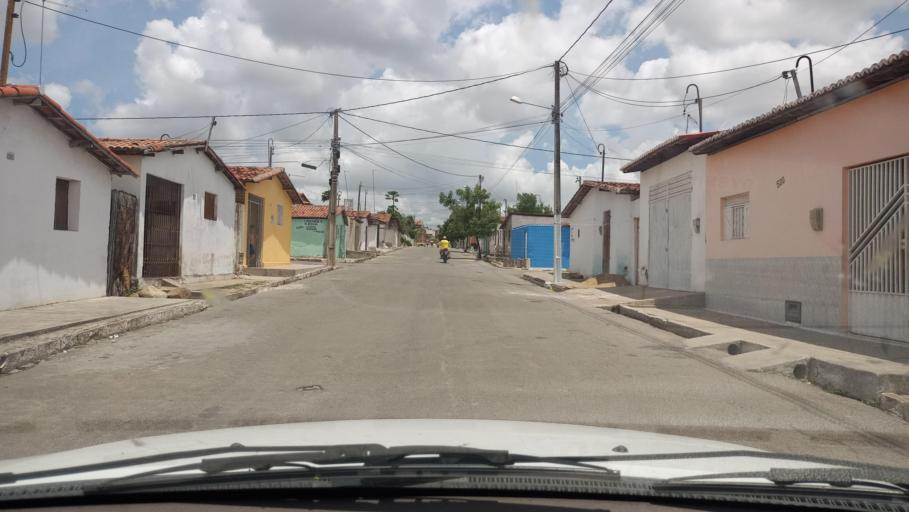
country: BR
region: Rio Grande do Norte
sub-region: Tangara
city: Tangara
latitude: -6.1011
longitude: -35.7101
